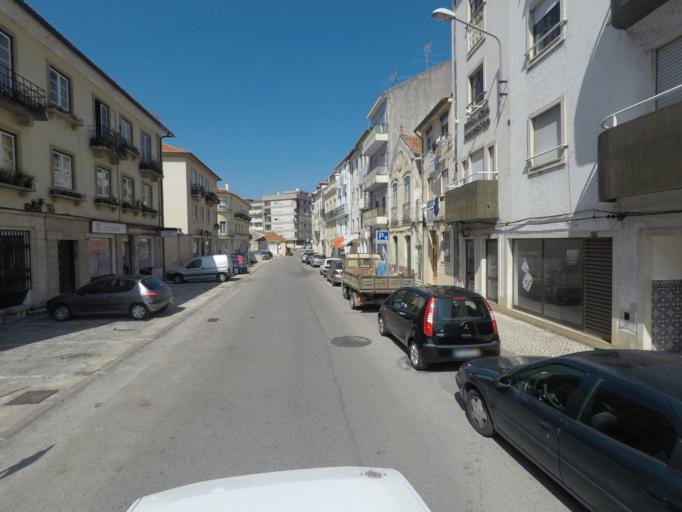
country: PT
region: Coimbra
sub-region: Coimbra
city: Coimbra
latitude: 40.2156
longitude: -8.4338
